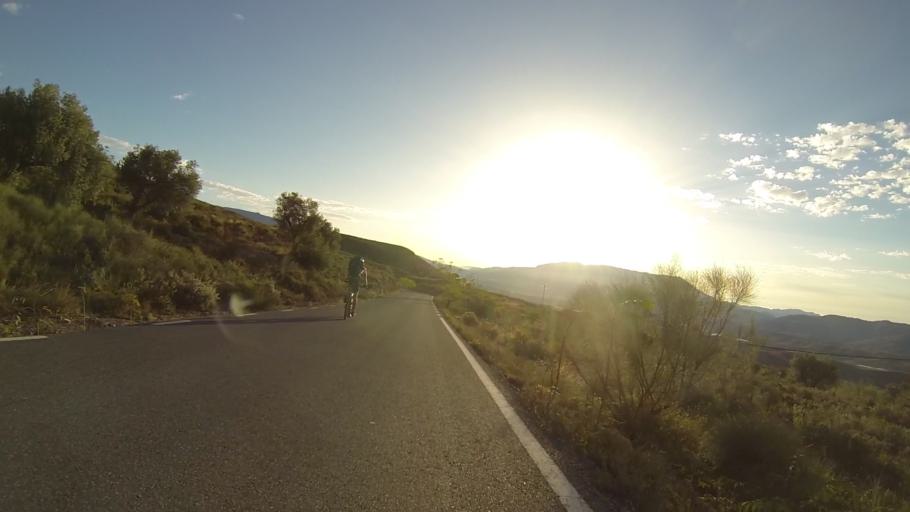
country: ES
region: Andalusia
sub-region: Provincia de Granada
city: Valor
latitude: 36.9780
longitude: -3.1318
